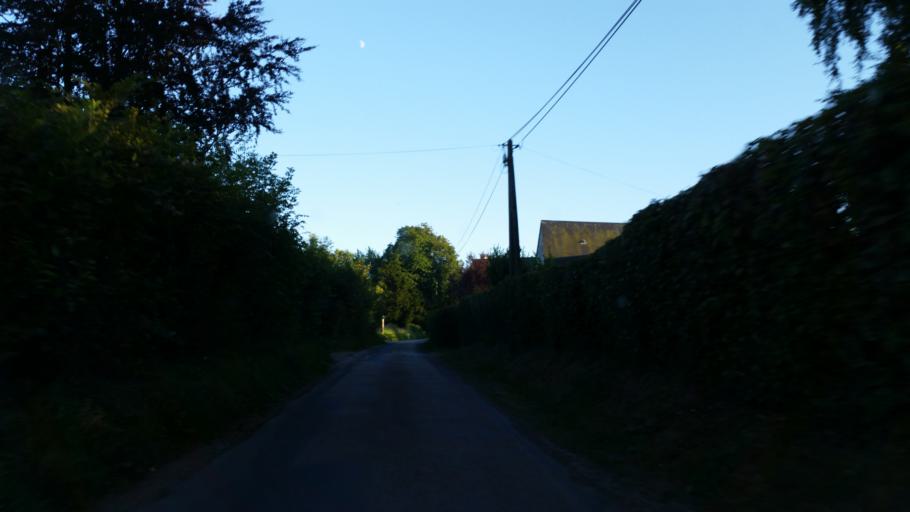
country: FR
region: Lower Normandy
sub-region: Departement du Calvados
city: Equemauville
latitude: 49.3807
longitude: 0.2284
